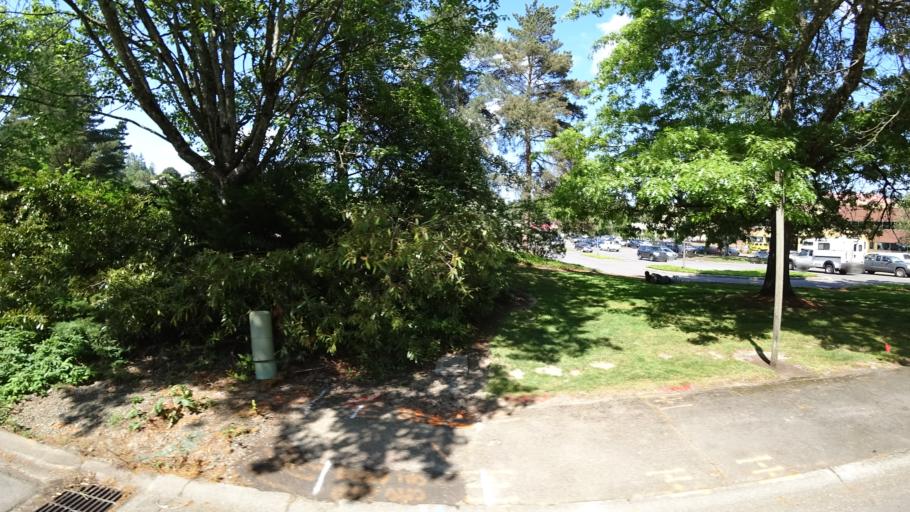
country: US
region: Oregon
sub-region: Clackamas County
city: Lake Oswego
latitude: 45.4333
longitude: -122.7058
